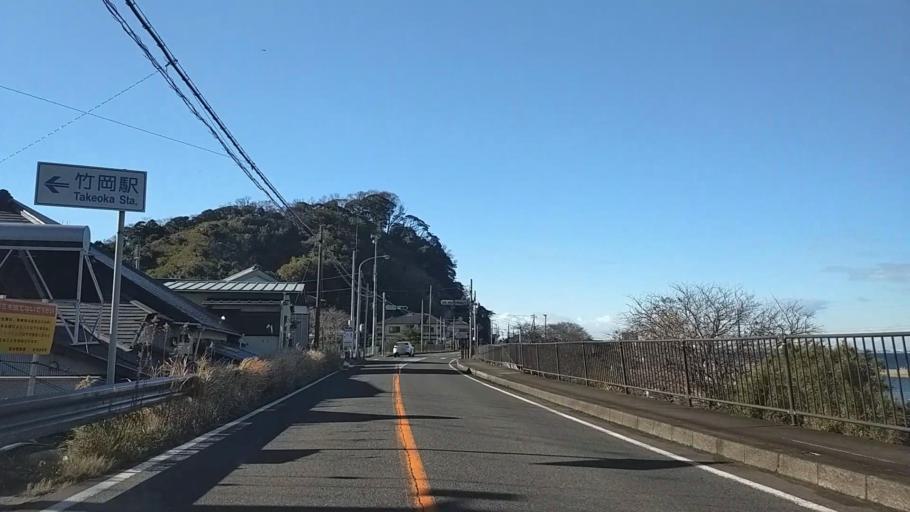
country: JP
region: Chiba
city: Futtsu
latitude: 35.1991
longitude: 139.8293
